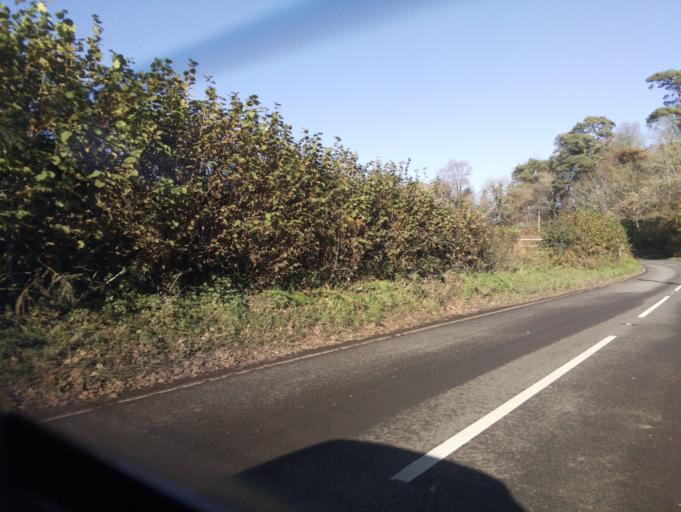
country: GB
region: England
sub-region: Dorset
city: Sherborne
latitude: 50.8444
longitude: -2.4900
